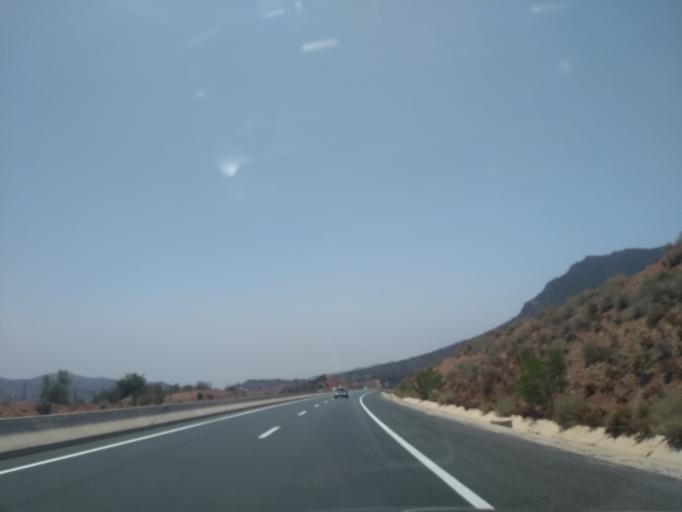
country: MA
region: Souss-Massa-Draa
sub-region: Taroudannt
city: Bigoudine
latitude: 30.5839
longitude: -9.3457
